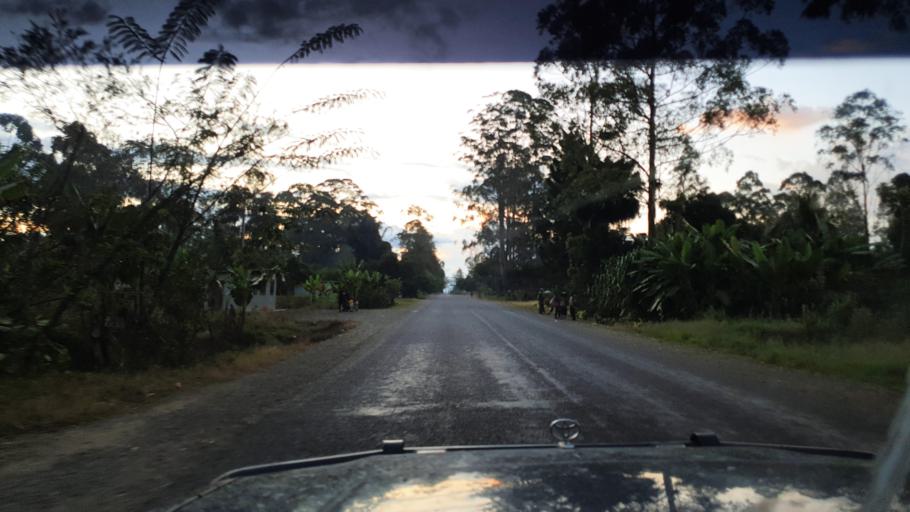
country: PG
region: Jiwaka
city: Minj
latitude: -5.8306
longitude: 144.5058
